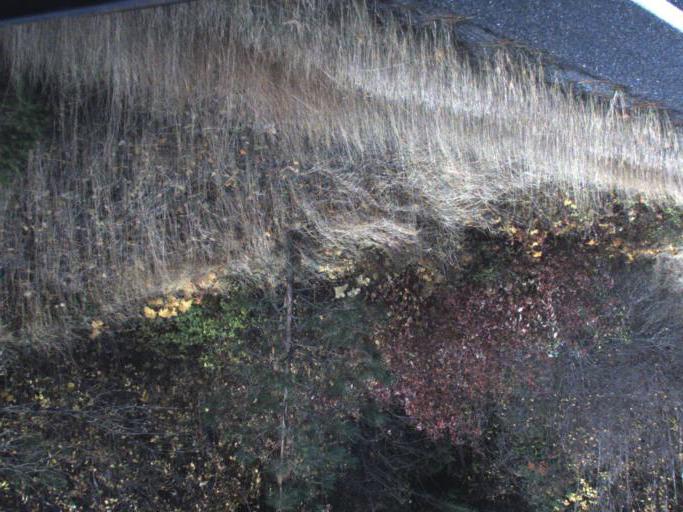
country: US
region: Washington
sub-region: Stevens County
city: Kettle Falls
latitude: 48.5260
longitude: -118.1366
